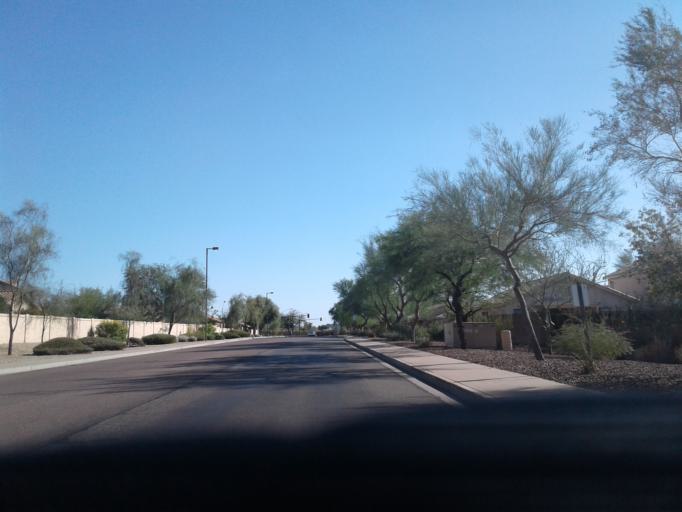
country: US
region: Arizona
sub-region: Maricopa County
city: Cave Creek
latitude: 33.6897
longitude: -112.0356
